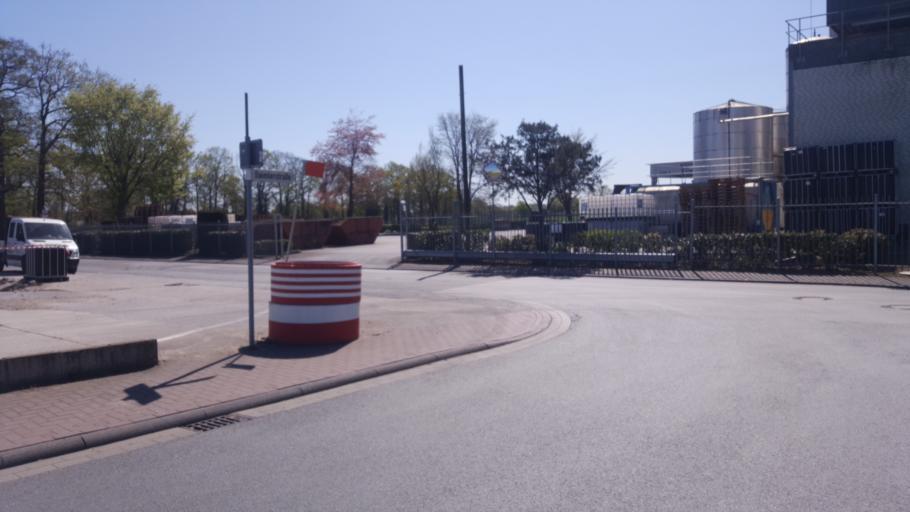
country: DE
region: North Rhine-Westphalia
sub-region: Regierungsbezirk Munster
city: Sudlohn
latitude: 51.9356
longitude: 6.8238
